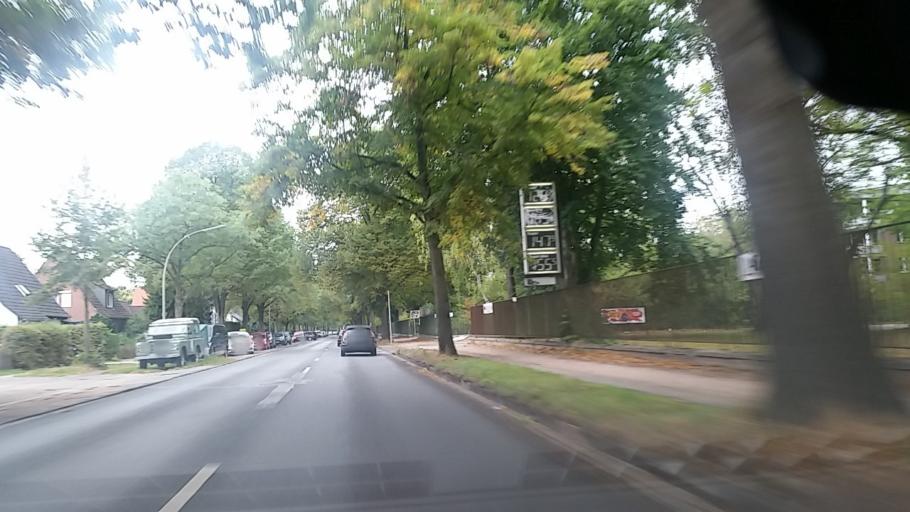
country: DE
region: Hamburg
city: Alsterdorf
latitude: 53.6164
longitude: 10.0133
